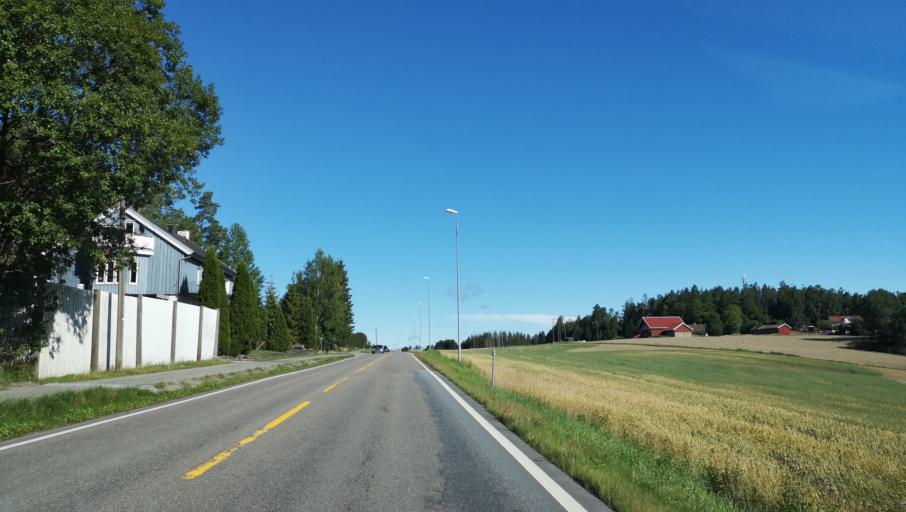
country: NO
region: Ostfold
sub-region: Spydeberg
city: Spydeberg
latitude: 59.5912
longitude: 11.1110
